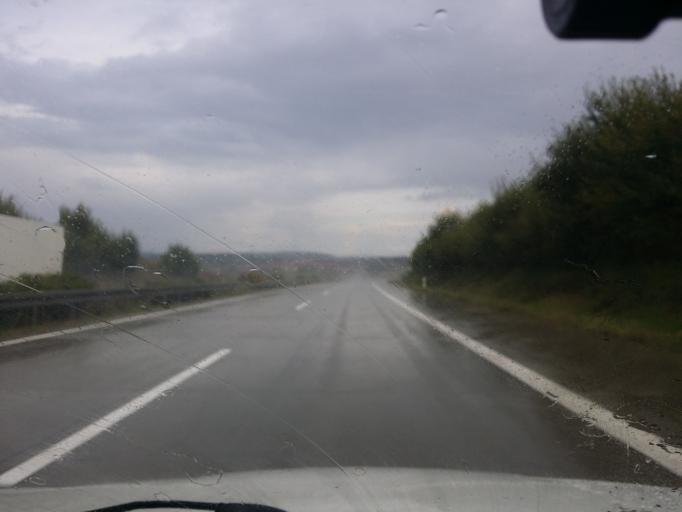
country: DE
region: Thuringia
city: Leinefelde
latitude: 51.3990
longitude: 10.3115
